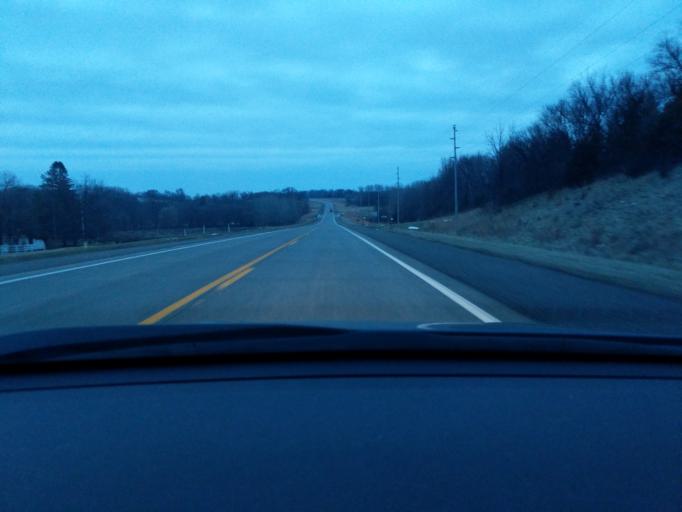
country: US
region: Minnesota
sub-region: Yellow Medicine County
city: Granite Falls
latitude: 44.7948
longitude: -95.4570
